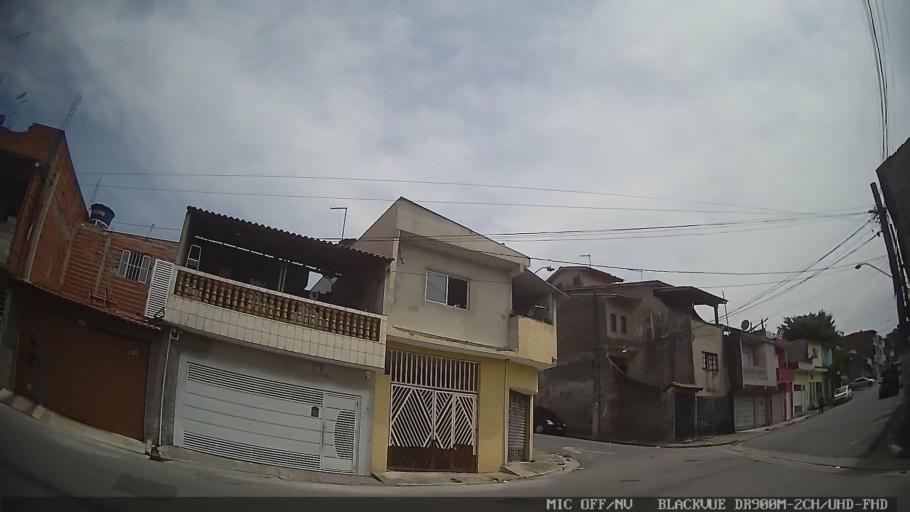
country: BR
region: Sao Paulo
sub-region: Ferraz De Vasconcelos
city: Ferraz de Vasconcelos
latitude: -23.5547
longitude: -46.3872
